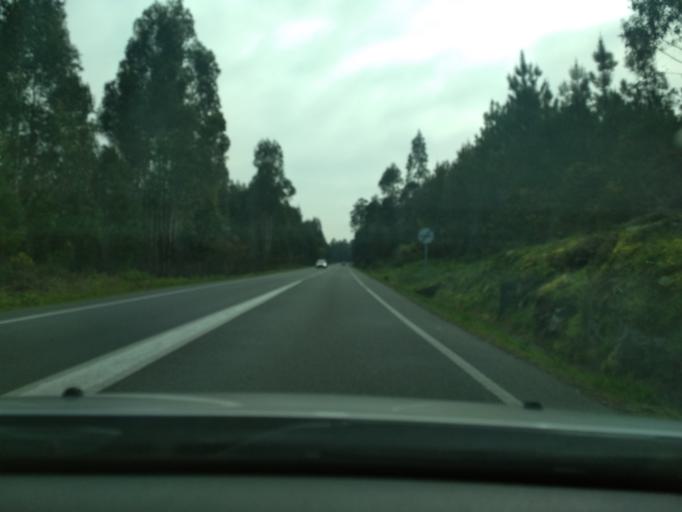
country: ES
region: Galicia
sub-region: Provincia de Pontevedra
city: Catoira
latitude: 42.6529
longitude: -8.7029
